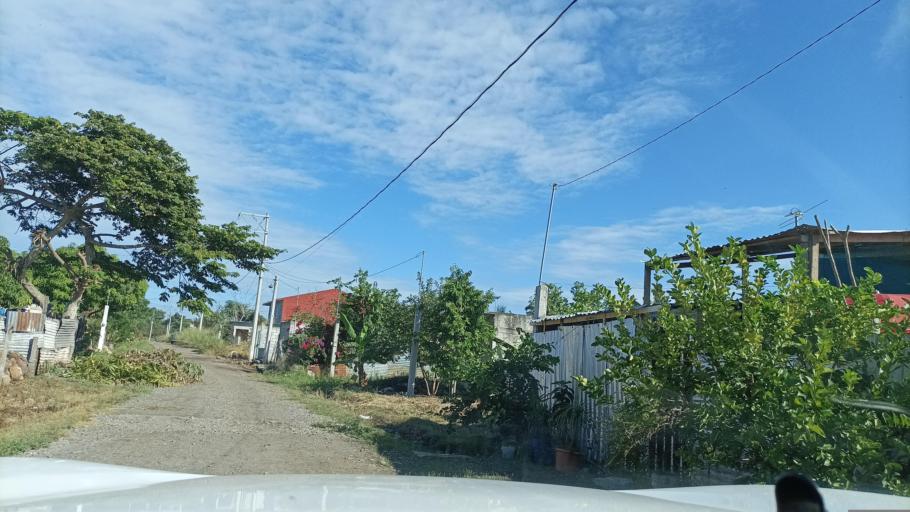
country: MX
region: Veracruz
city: Paso del Macho
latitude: 18.9703
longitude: -96.7138
